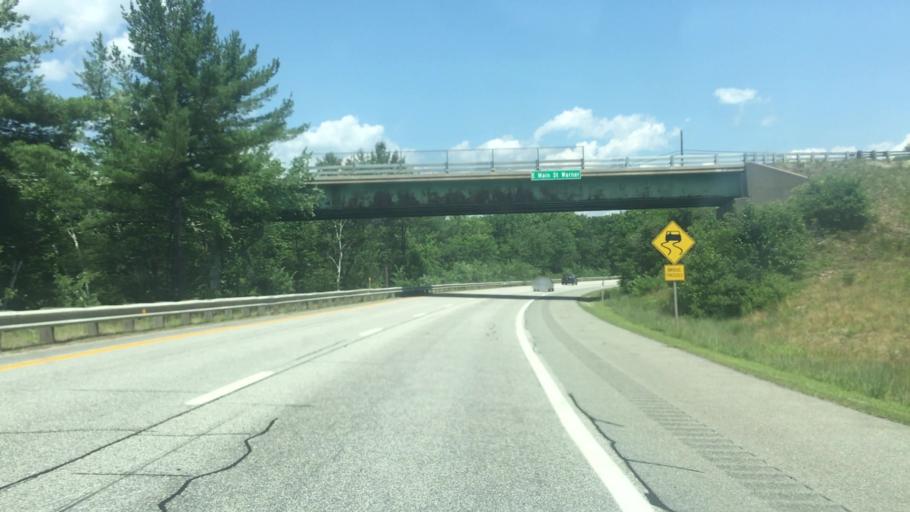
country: US
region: New Hampshire
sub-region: Merrimack County
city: Contoocook
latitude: 43.2723
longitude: -71.7932
